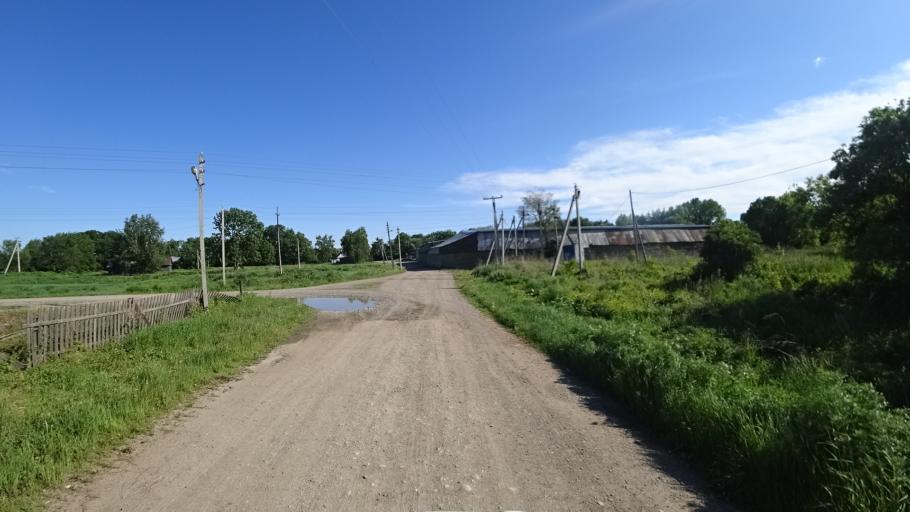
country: RU
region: Khabarovsk Krai
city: Khor
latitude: 47.8877
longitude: 134.9985
